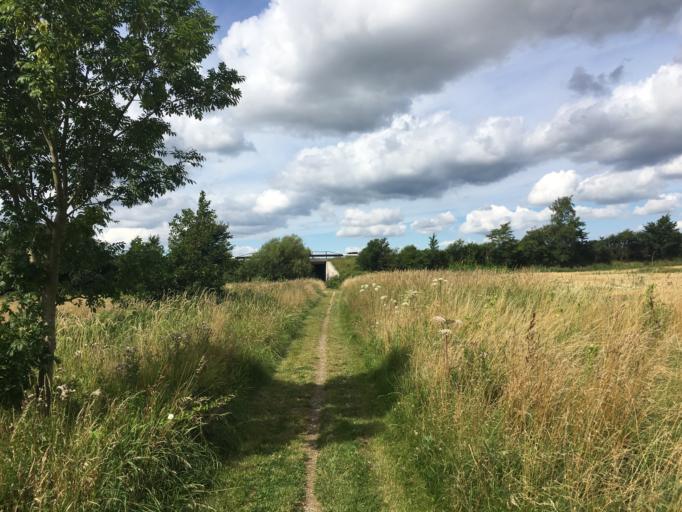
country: DK
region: Capital Region
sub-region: Fredensborg Kommune
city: Niva
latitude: 55.9320
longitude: 12.4809
